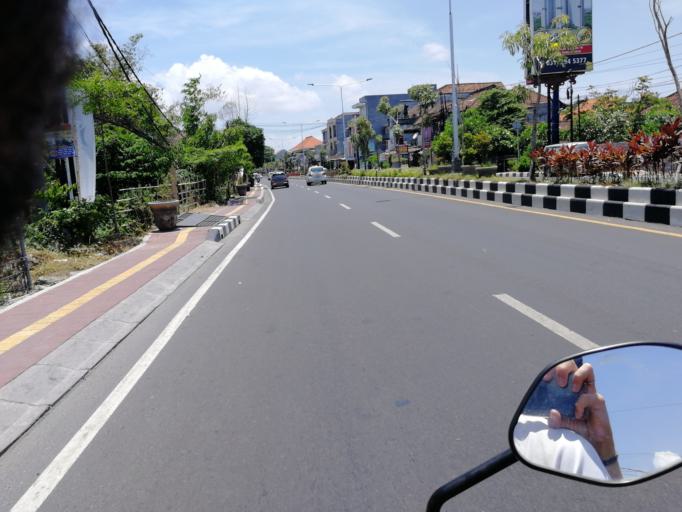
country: ID
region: Bali
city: Kuta
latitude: -8.6953
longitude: 115.1872
